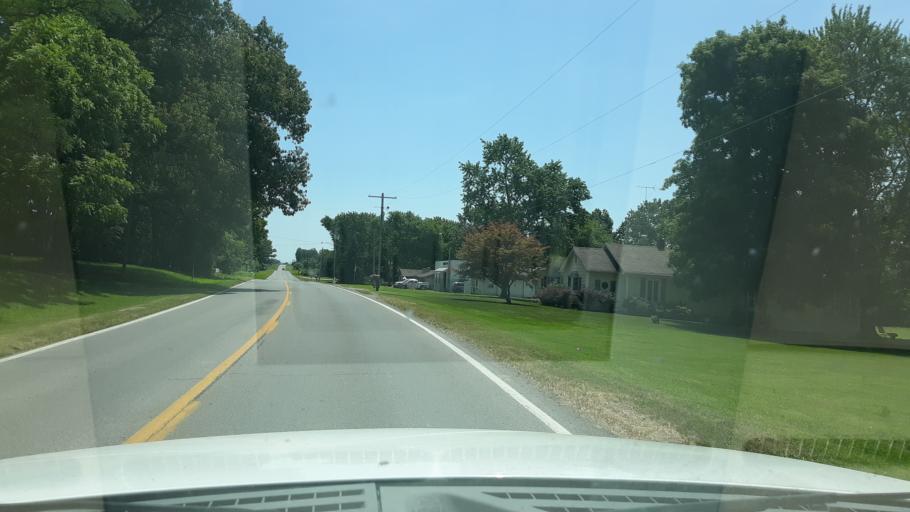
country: US
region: Illinois
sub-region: Saline County
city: Eldorado
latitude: 37.8048
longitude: -88.4374
